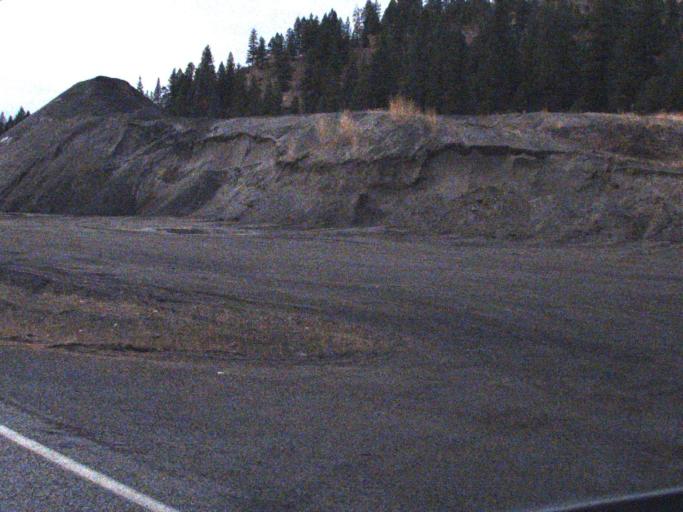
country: US
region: Washington
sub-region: Ferry County
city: Republic
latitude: 48.5971
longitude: -118.6423
